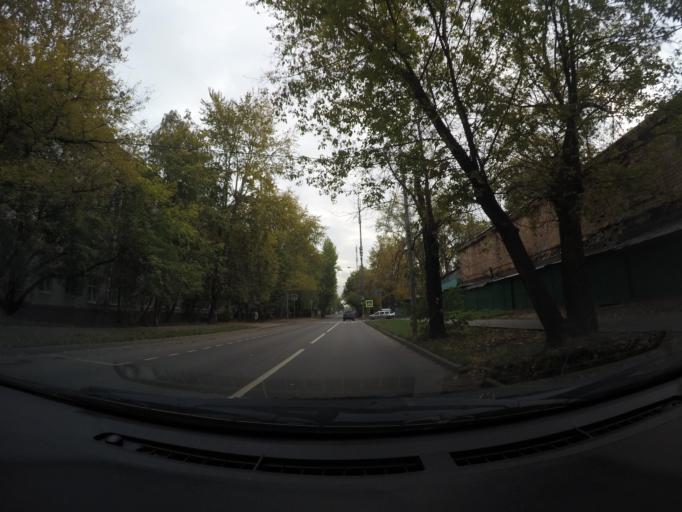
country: RU
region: Moscow
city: Lefortovo
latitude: 55.7631
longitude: 37.7292
